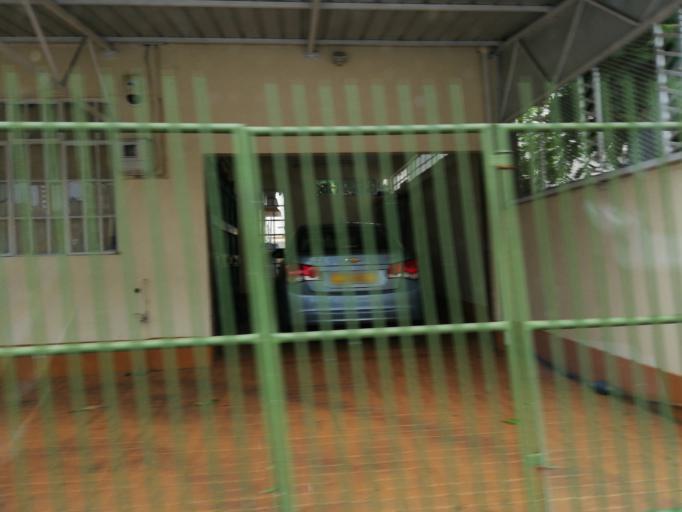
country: MU
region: Black River
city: Gros Cailloux
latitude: -20.2329
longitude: 57.4546
